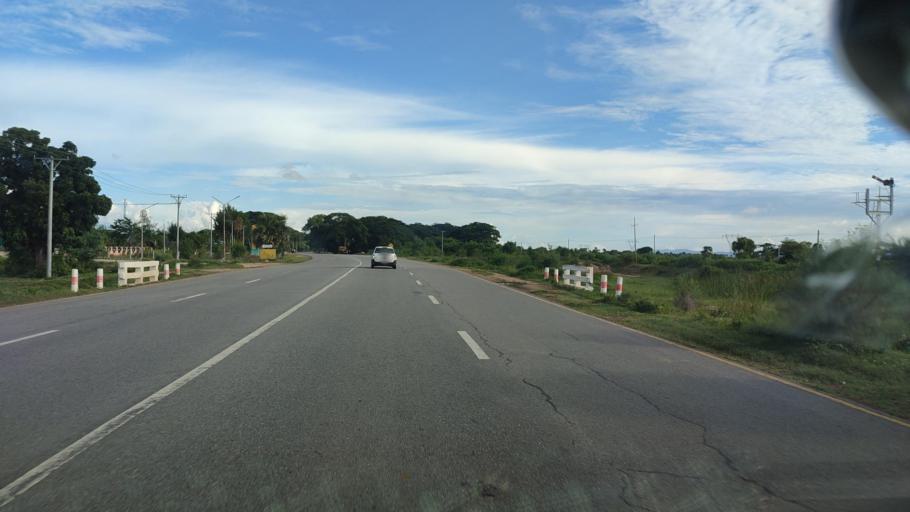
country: MM
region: Mandalay
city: Yamethin
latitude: 20.1944
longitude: 96.1835
